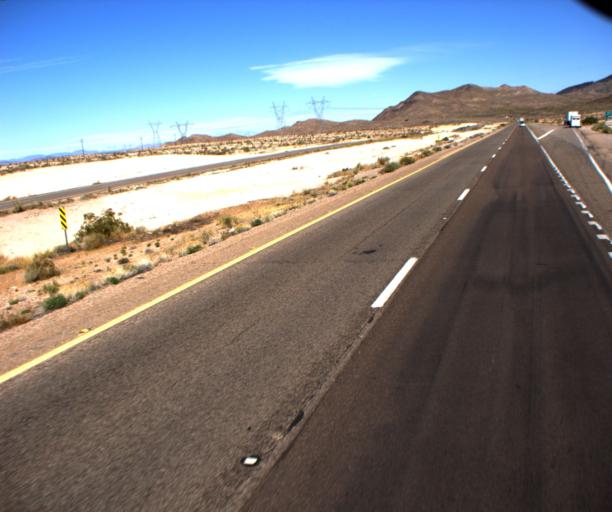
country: US
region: Nevada
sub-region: Clark County
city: Boulder City
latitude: 35.8345
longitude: -114.5652
